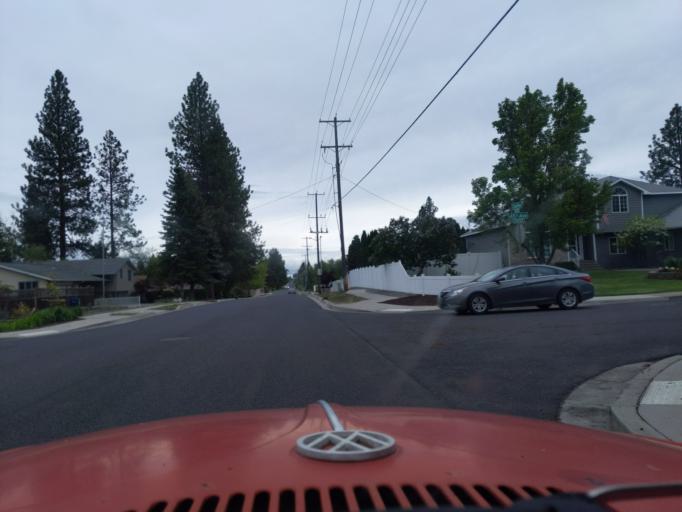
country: US
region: Washington
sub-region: Spokane County
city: Spokane
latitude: 47.6122
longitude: -117.3790
